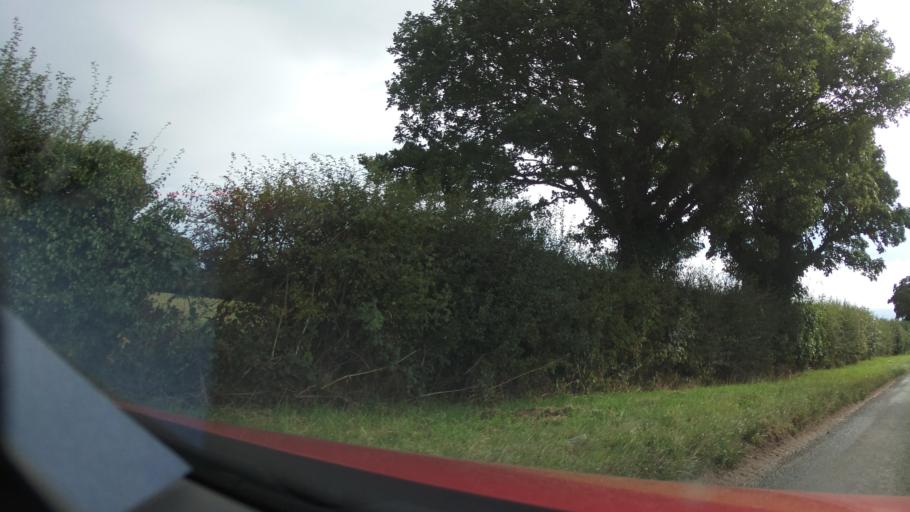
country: GB
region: England
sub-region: Shropshire
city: Shifnal
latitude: 52.6900
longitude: -2.3598
